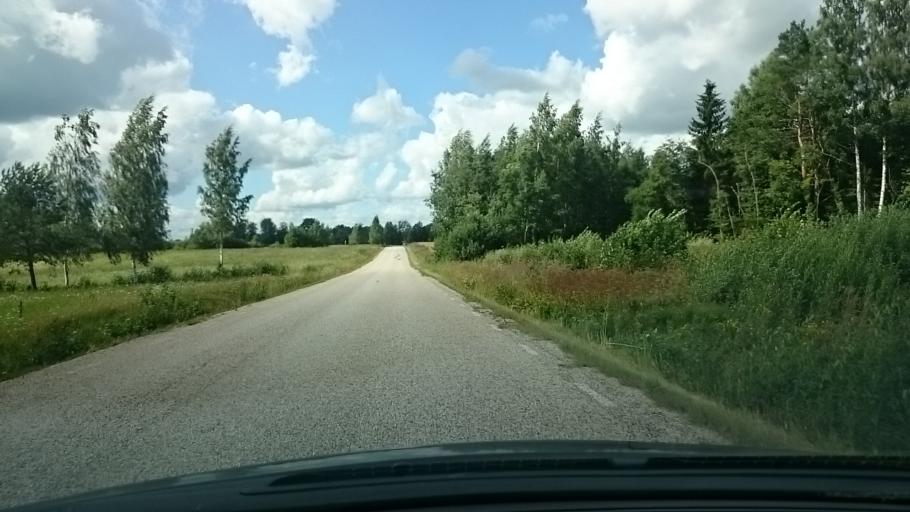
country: EE
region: Vorumaa
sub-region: Voru linn
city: Voru
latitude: 57.9201
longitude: 27.1420
